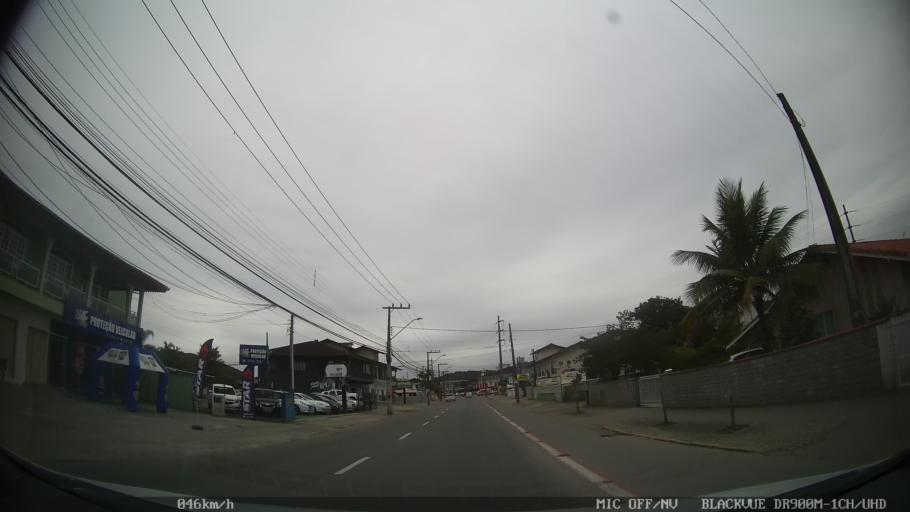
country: BR
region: Santa Catarina
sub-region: Joinville
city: Joinville
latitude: -26.2705
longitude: -48.8169
